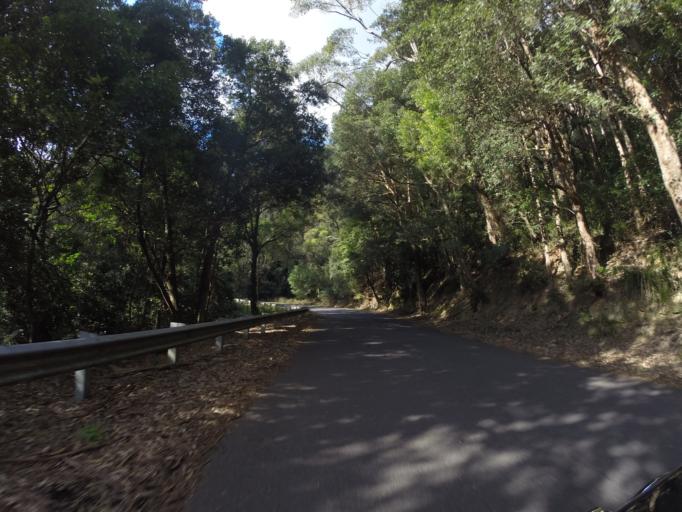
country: AU
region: New South Wales
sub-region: Wollongong
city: Mount Keira
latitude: -34.4007
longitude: 150.8524
